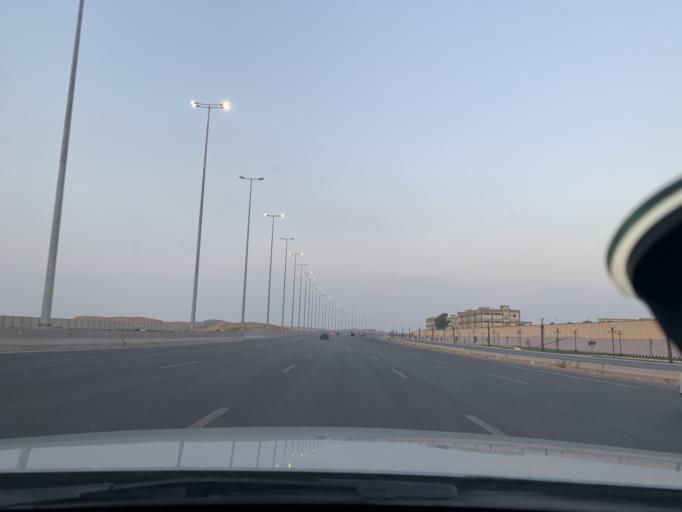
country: EG
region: Muhafazat al Qalyubiyah
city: Al Khankah
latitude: 30.0926
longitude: 31.4736
